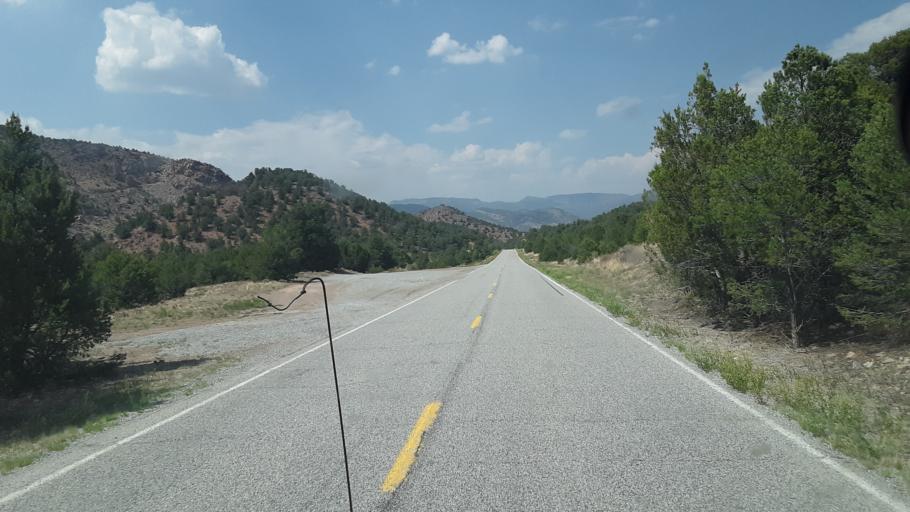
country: US
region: Colorado
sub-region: Custer County
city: Westcliffe
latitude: 38.3701
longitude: -105.5852
